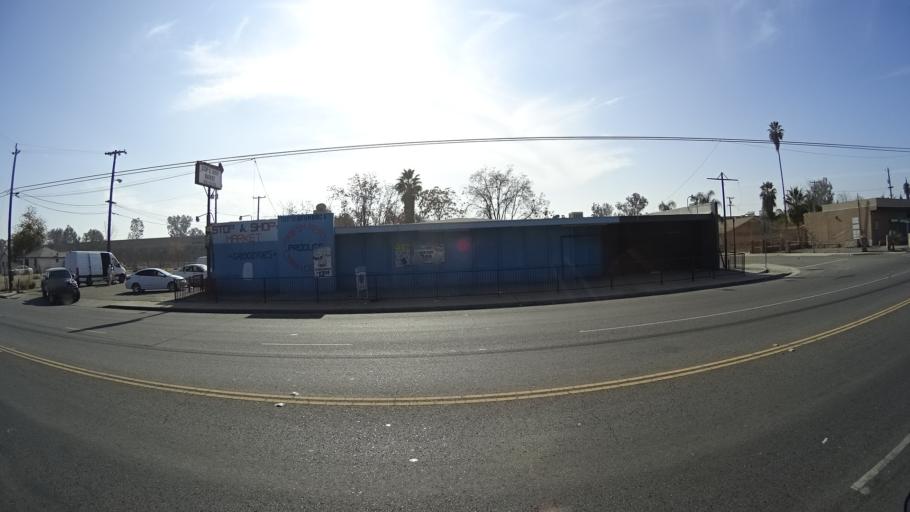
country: US
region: California
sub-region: Kern County
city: Bakersfield
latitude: 35.3540
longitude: -118.9928
